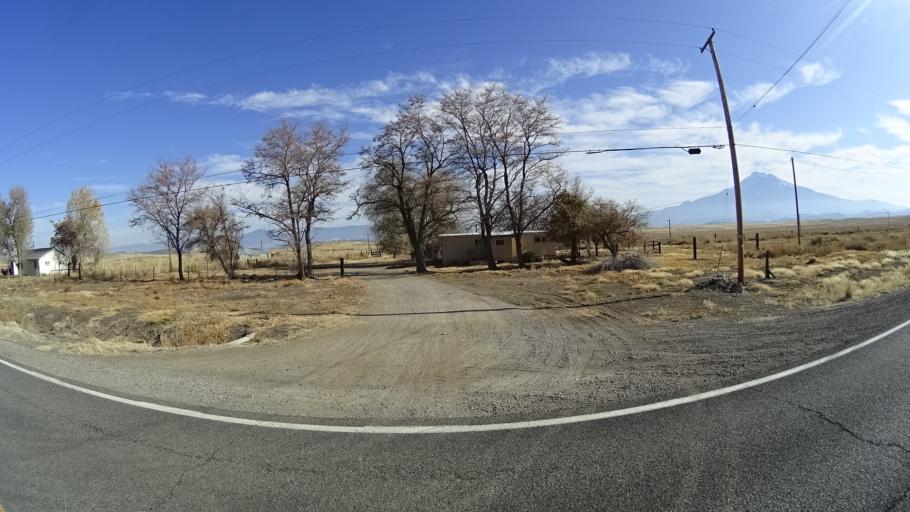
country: US
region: California
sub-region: Siskiyou County
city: Weed
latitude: 41.5007
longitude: -122.5143
